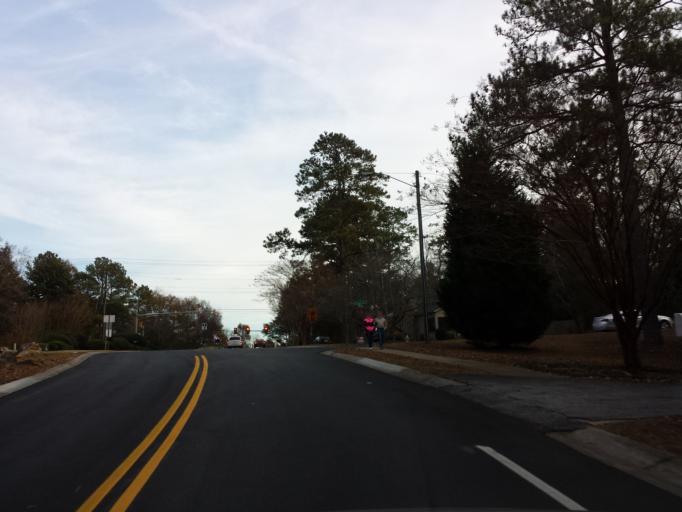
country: US
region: Georgia
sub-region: Fulton County
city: Sandy Springs
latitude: 33.9611
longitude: -84.4315
